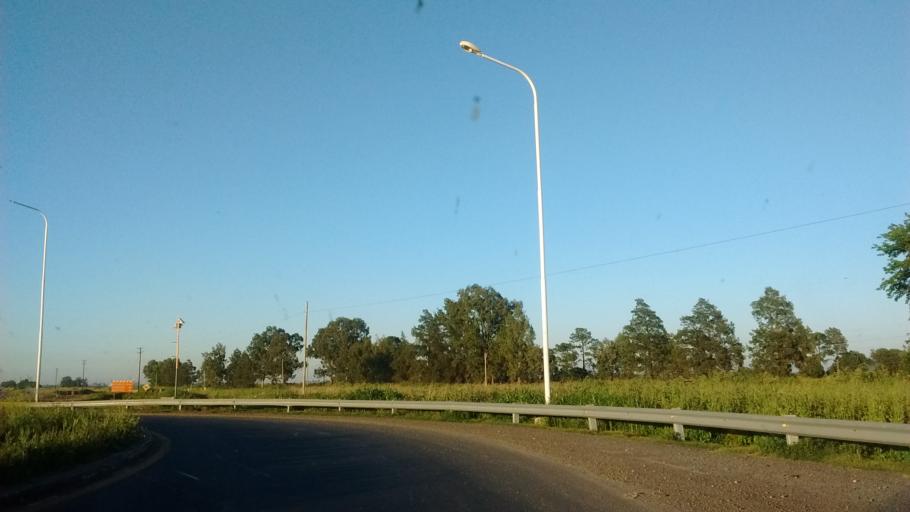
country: AR
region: Santa Fe
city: Casilda
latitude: -33.1996
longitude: -61.3229
